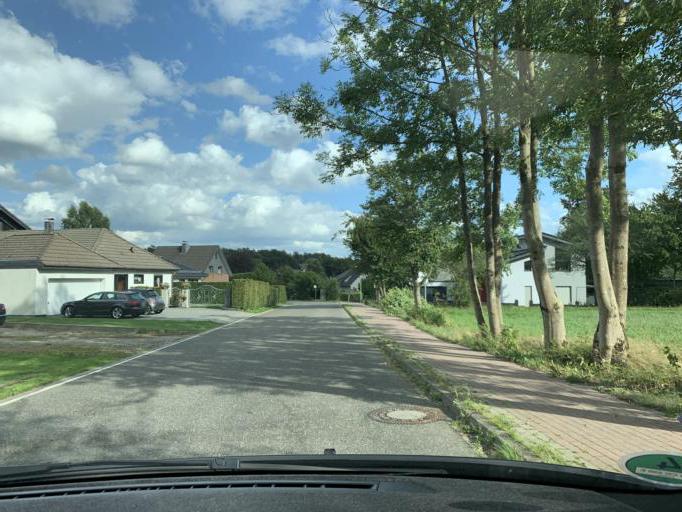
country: DE
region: North Rhine-Westphalia
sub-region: Regierungsbezirk Koln
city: Monschau
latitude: 50.5916
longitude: 6.2490
